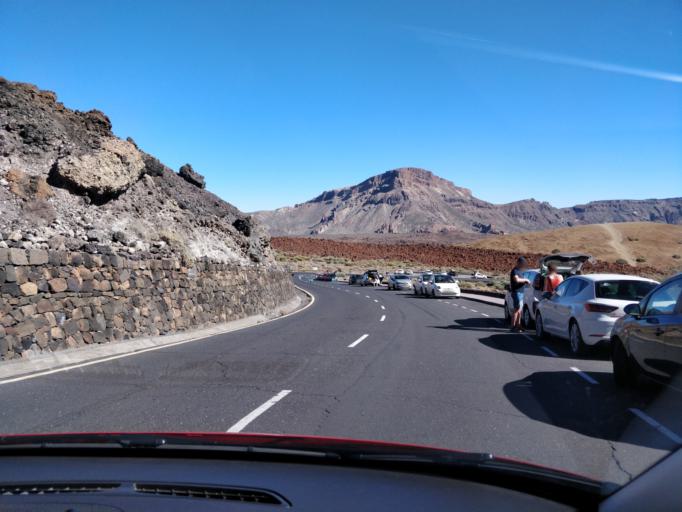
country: ES
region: Canary Islands
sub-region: Provincia de Santa Cruz de Tenerife
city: Vilaflor
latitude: 28.2560
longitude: -16.6230
